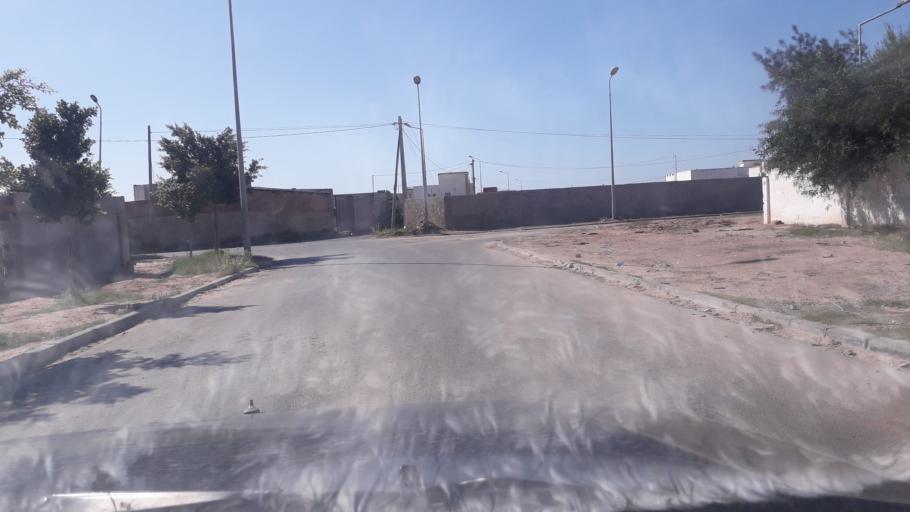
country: TN
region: Safaqis
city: Al Qarmadah
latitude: 34.8245
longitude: 10.7507
